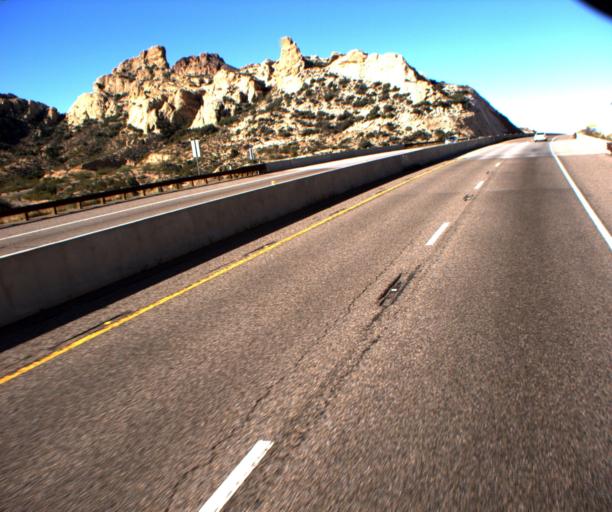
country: US
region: Arizona
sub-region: Mohave County
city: Golden Valley
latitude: 35.2206
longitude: -114.3889
